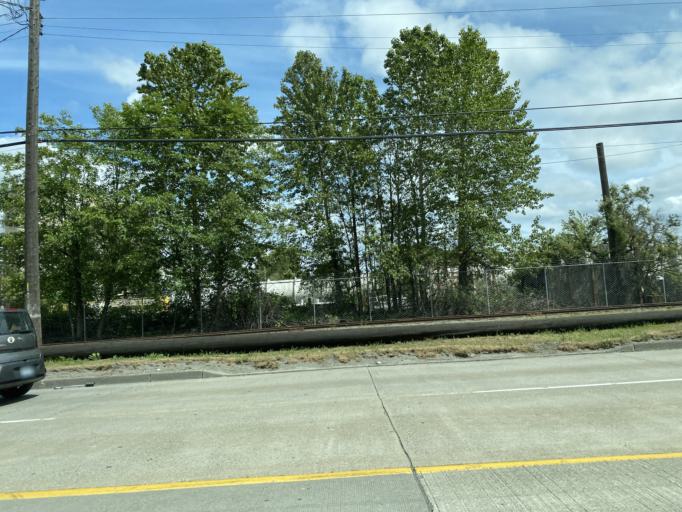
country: US
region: Washington
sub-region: King County
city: White Center
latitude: 47.5490
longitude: -122.3455
